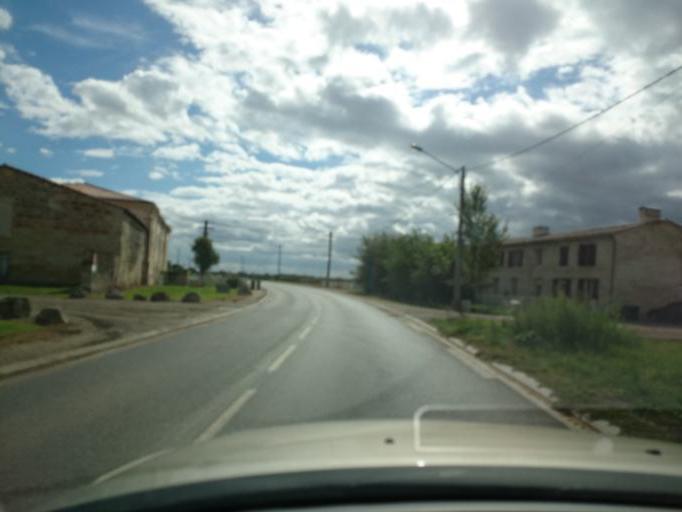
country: FR
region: Aquitaine
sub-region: Departement de la Gironde
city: Saint-Louis-de-Montferrand
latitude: 44.9307
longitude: -0.5623
